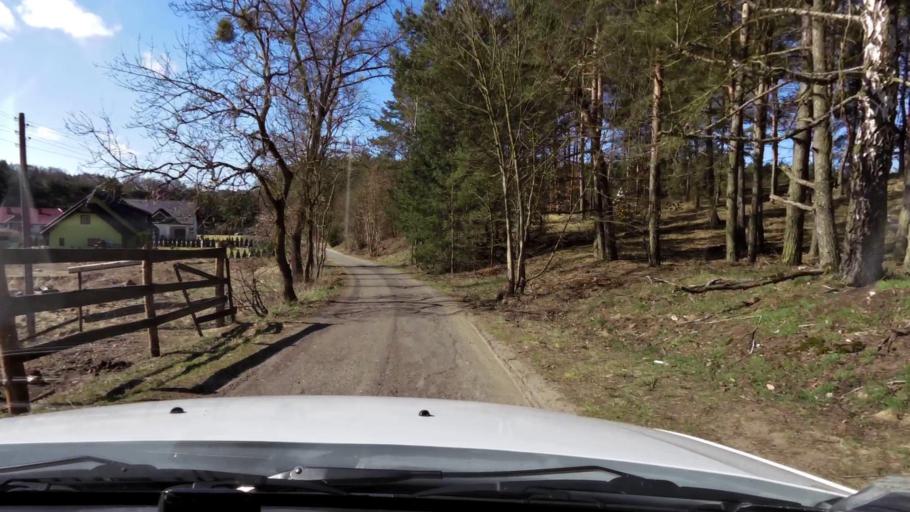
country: PL
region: West Pomeranian Voivodeship
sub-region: Powiat gryfinski
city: Gryfino
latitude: 53.2199
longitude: 14.5172
